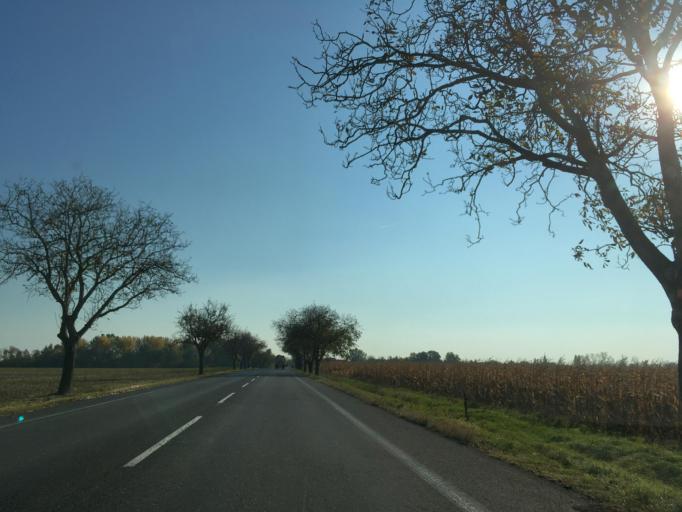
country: SK
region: Trnavsky
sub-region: Okres Dunajska Streda
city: Velky Meder
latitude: 47.8127
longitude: 17.8387
